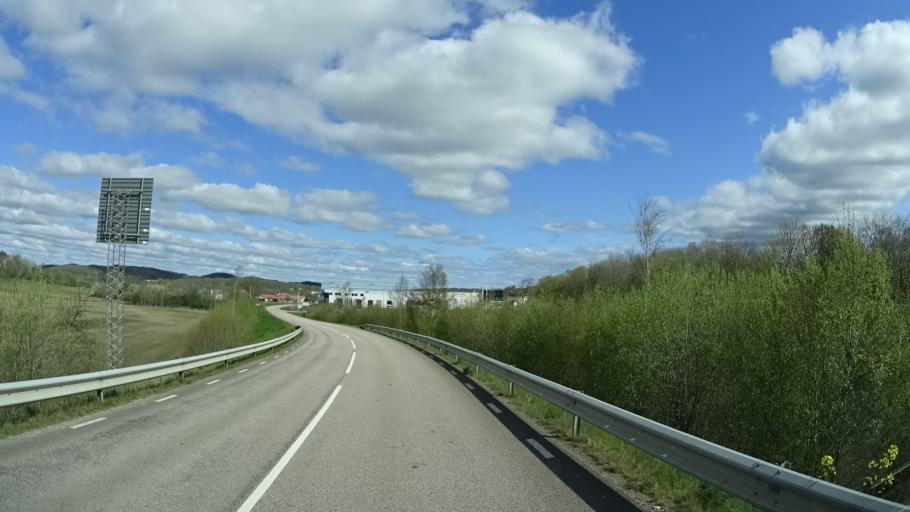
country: SE
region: Halland
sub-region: Halmstads Kommun
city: Getinge
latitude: 56.8525
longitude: 12.6815
